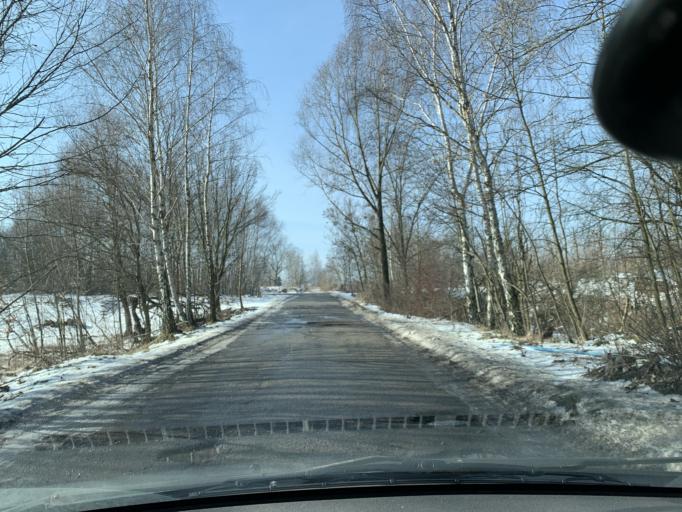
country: PL
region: Silesian Voivodeship
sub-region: Powiat tarnogorski
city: Radzionkow
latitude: 50.3666
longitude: 18.8831
